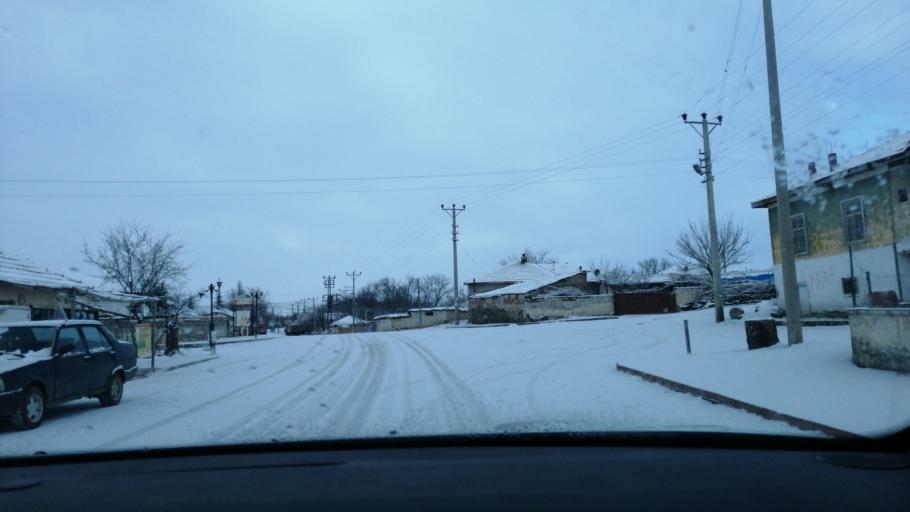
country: TR
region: Aksaray
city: Agacoren
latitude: 38.9328
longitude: 33.9489
